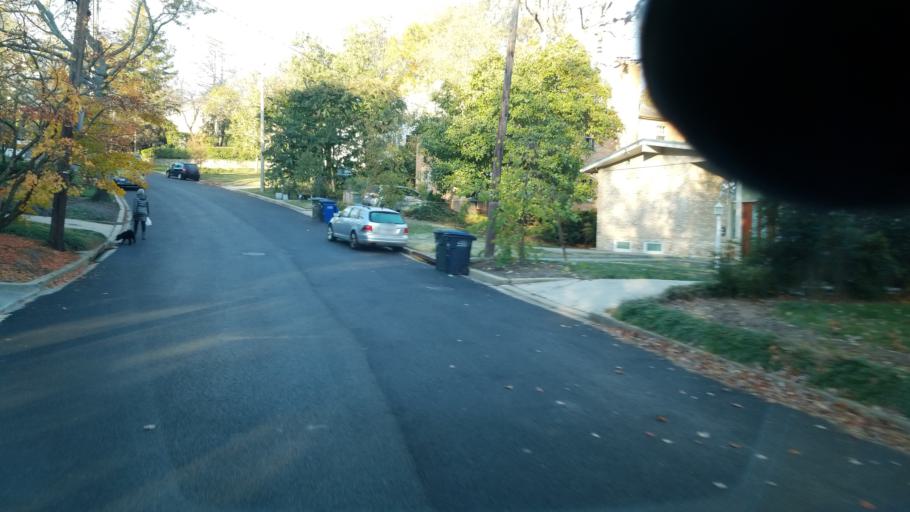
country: US
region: Maryland
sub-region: Montgomery County
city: Chevy Chase
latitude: 38.9537
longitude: -77.0590
